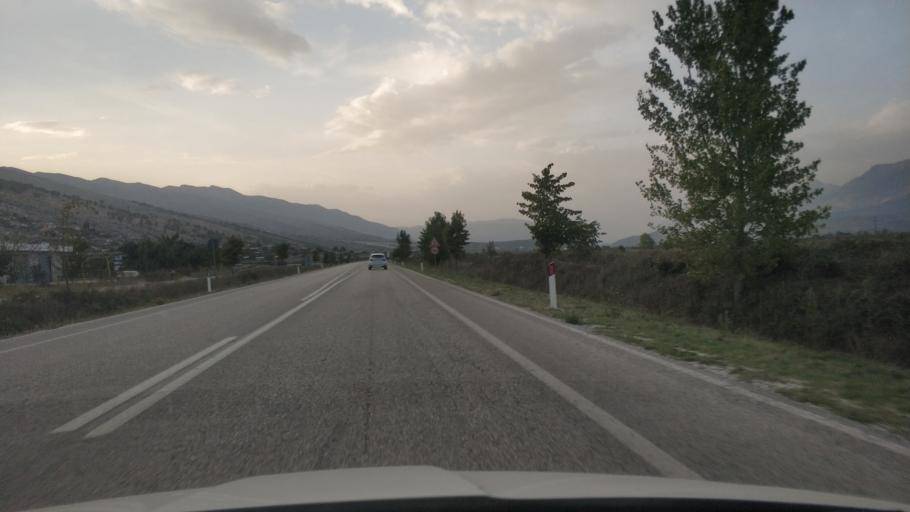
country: AL
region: Gjirokaster
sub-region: Rrethi i Gjirokastres
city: Dervician
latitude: 40.0111
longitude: 20.2028
